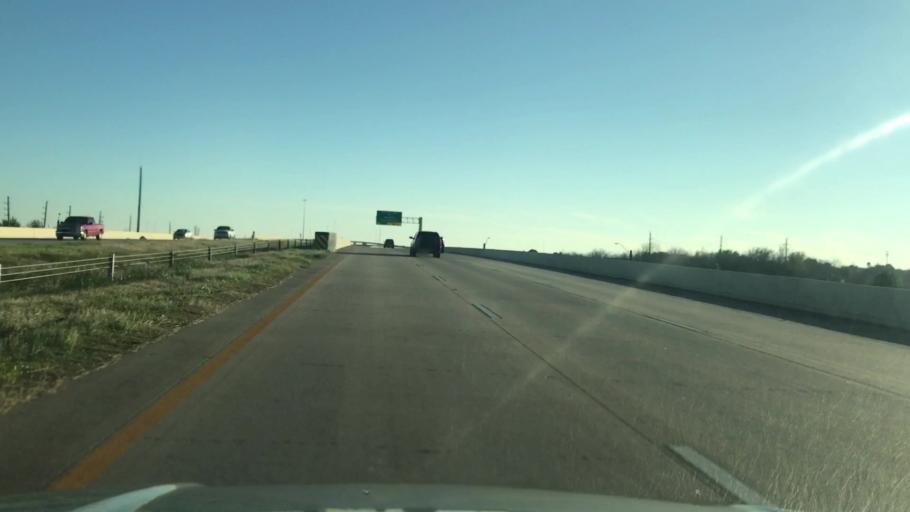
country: US
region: Texas
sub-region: Harris County
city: Katy
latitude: 29.8034
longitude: -95.7754
